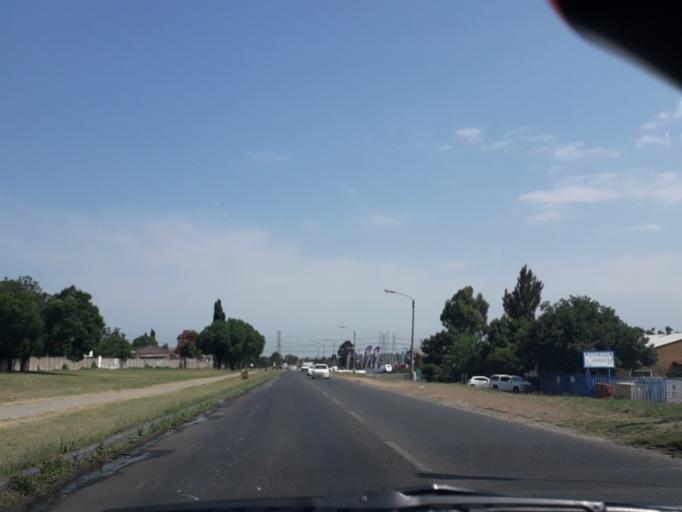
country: ZA
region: Gauteng
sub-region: City of Johannesburg Metropolitan Municipality
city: Modderfontein
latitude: -26.1233
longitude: 28.1727
